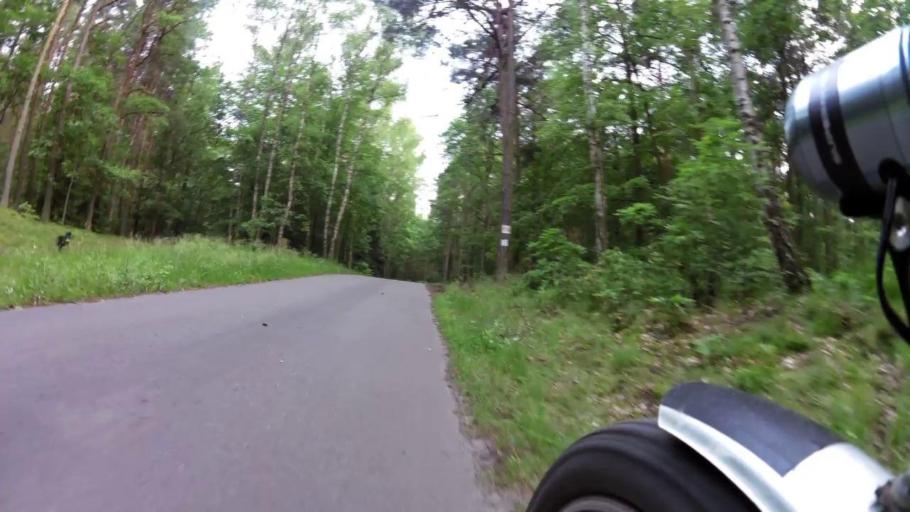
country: PL
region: West Pomeranian Voivodeship
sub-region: Powiat policki
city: Police
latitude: 53.6476
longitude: 14.4926
